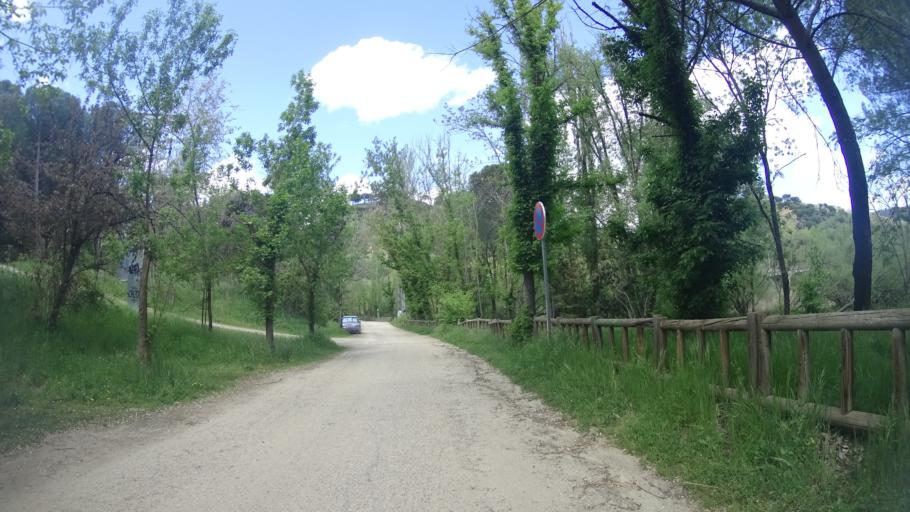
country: ES
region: Madrid
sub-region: Provincia de Madrid
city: Pelayos de la Presa
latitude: 40.3661
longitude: -4.3051
